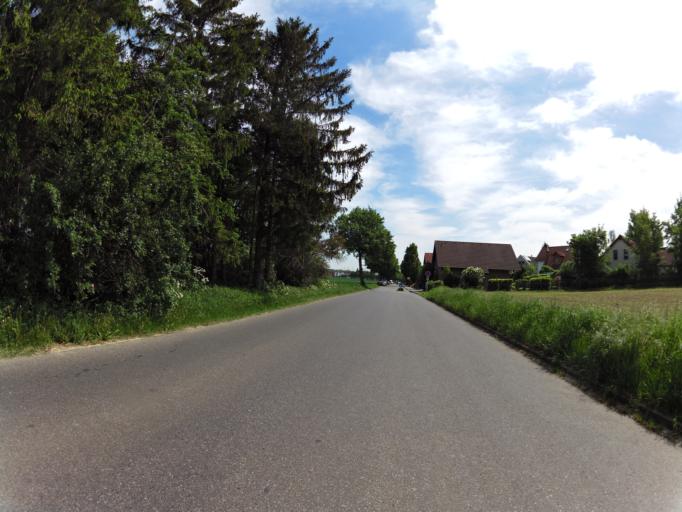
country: NL
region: Limburg
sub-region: Gemeente Kerkrade
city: Kerkrade
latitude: 50.8187
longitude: 6.0474
